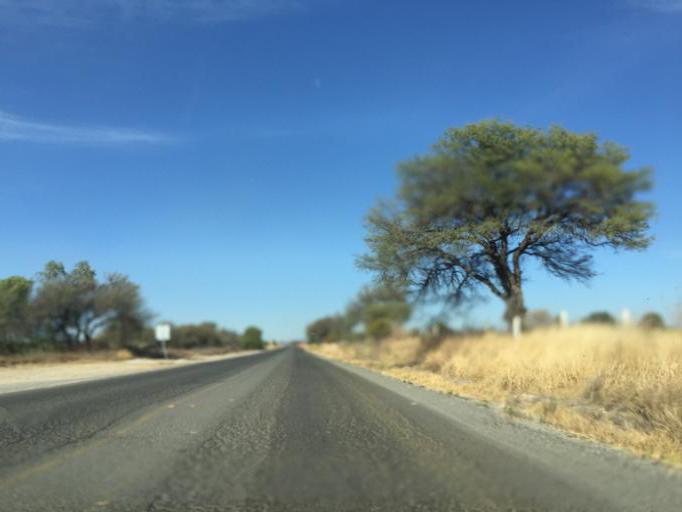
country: MX
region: Queretaro
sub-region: Colon
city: Los Benitos
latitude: 20.6727
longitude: -99.9352
